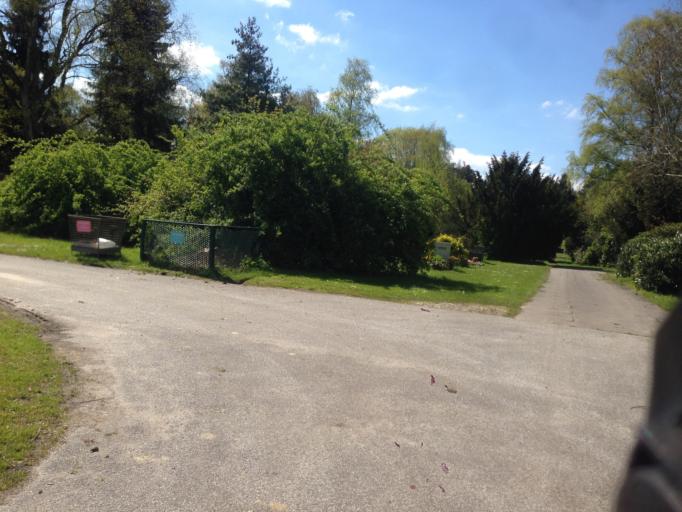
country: DE
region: Hamburg
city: Steilshoop
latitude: 53.6232
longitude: 10.0621
